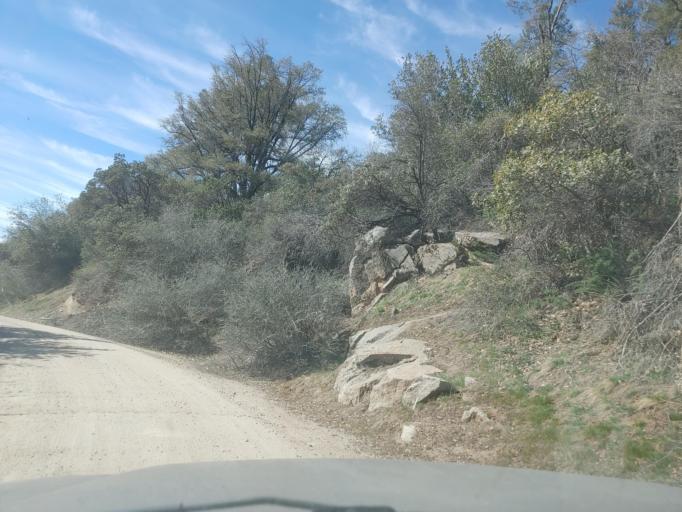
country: US
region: California
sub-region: Madera County
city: Ahwahnee
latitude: 37.4162
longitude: -119.6949
